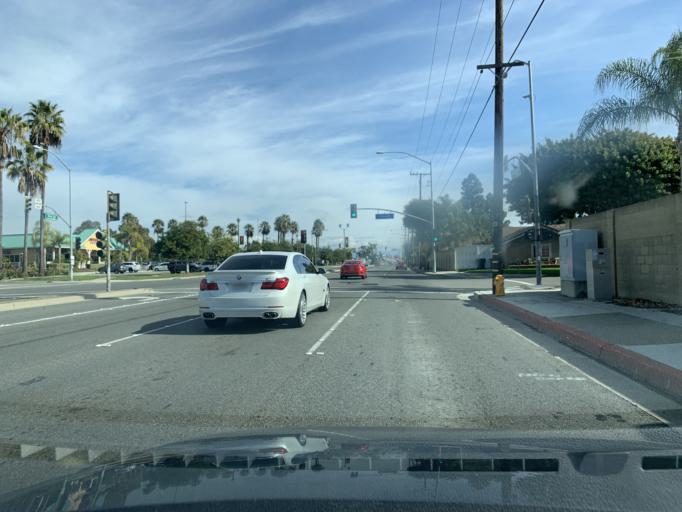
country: US
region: California
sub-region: Orange County
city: Westminster
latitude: 33.7443
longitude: -118.0118
